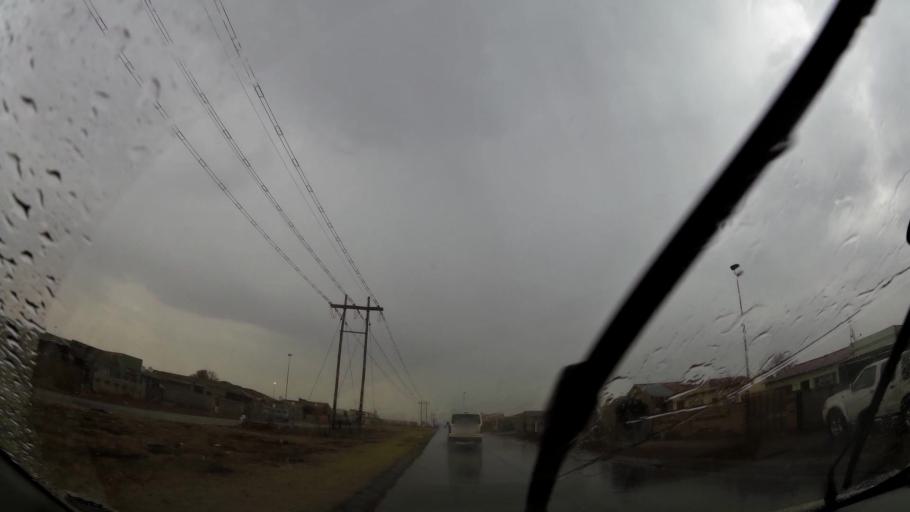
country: ZA
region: Gauteng
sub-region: Ekurhuleni Metropolitan Municipality
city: Germiston
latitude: -26.3589
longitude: 28.1483
